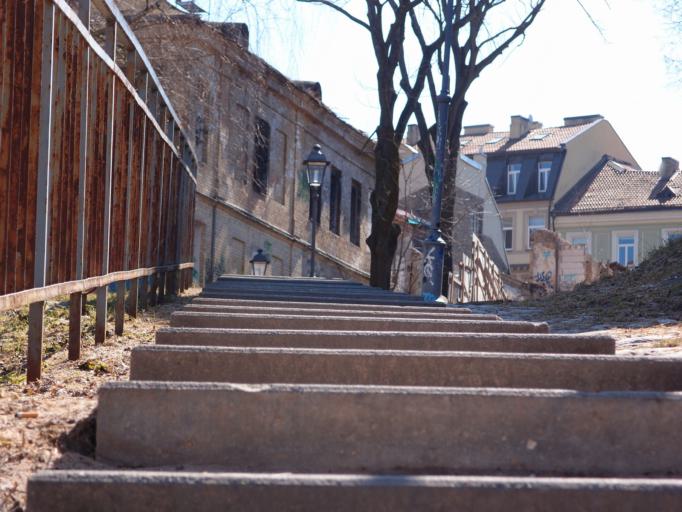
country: LT
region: Vilnius County
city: Rasos
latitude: 54.6814
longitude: 25.2969
